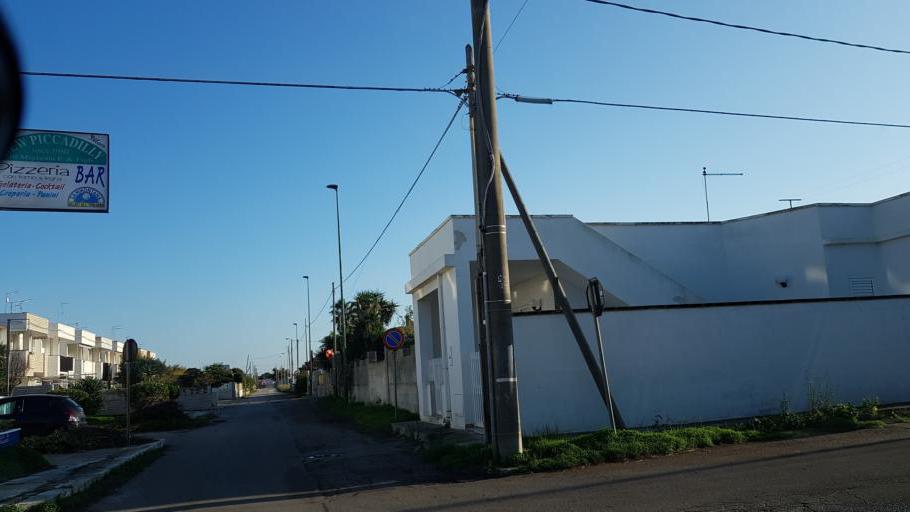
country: IT
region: Apulia
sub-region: Provincia di Brindisi
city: Torchiarolo
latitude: 40.5164
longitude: 18.0931
